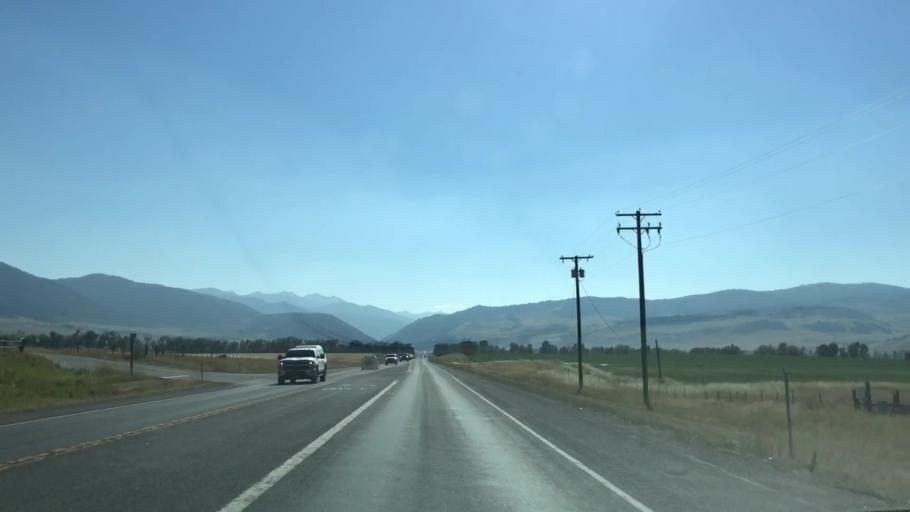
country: US
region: Montana
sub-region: Gallatin County
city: Four Corners
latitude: 45.5538
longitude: -111.2070
